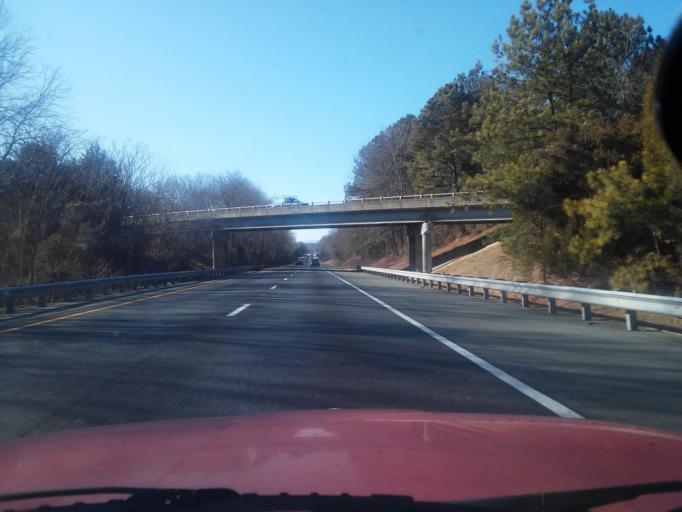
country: US
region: Virginia
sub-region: City of Charlottesville
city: Charlottesville
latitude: 38.0127
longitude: -78.3820
